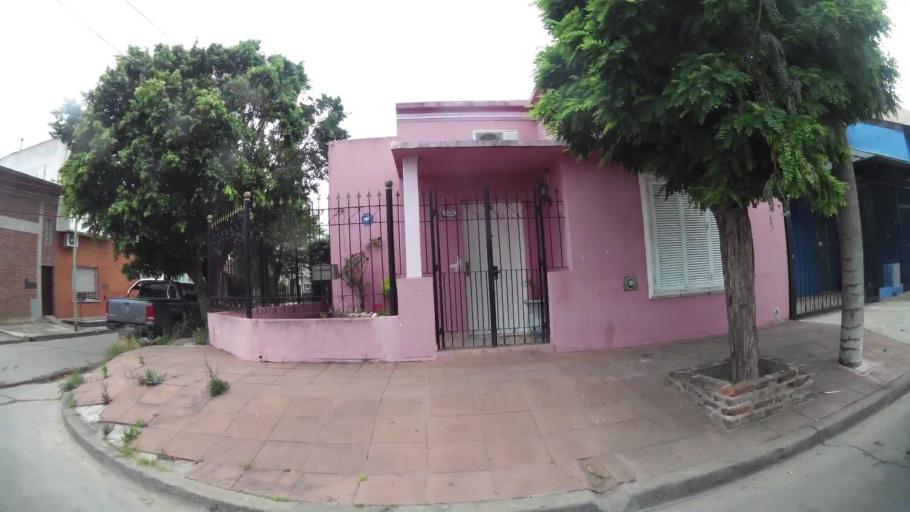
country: AR
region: Buenos Aires
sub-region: Partido de Zarate
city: Zarate
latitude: -34.1054
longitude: -59.0150
